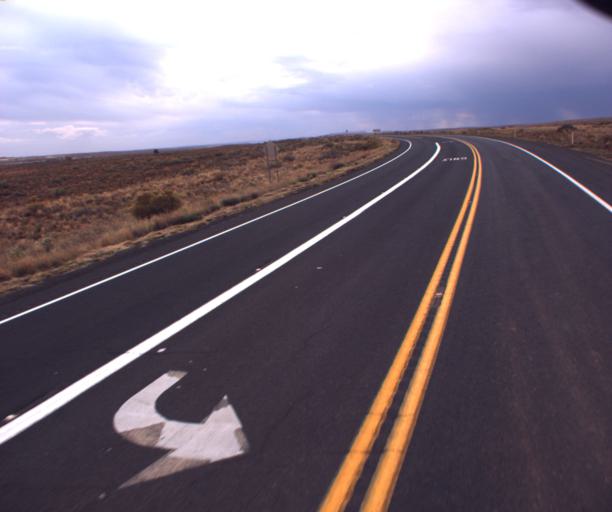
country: US
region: Arizona
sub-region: Coconino County
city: Kaibito
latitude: 36.3915
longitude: -110.8796
